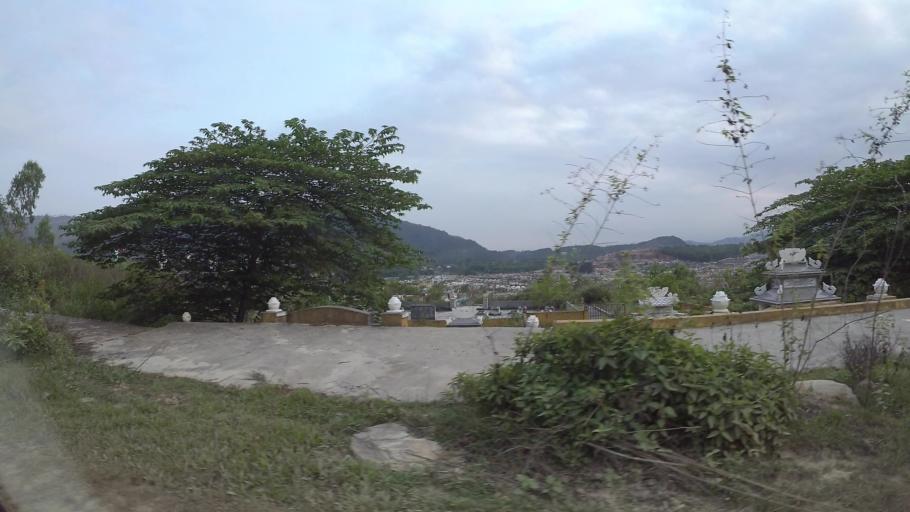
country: VN
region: Da Nang
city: Lien Chieu
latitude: 16.0625
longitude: 108.1143
